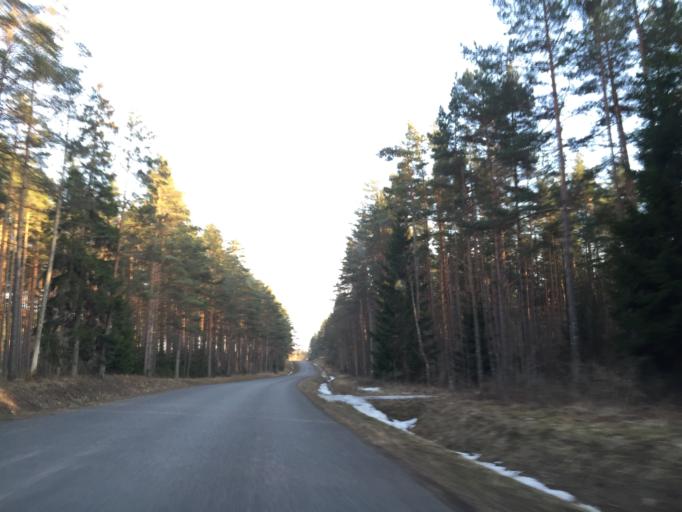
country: EE
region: Laeaene
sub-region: Lihula vald
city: Lihula
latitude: 58.4685
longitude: 23.7182
